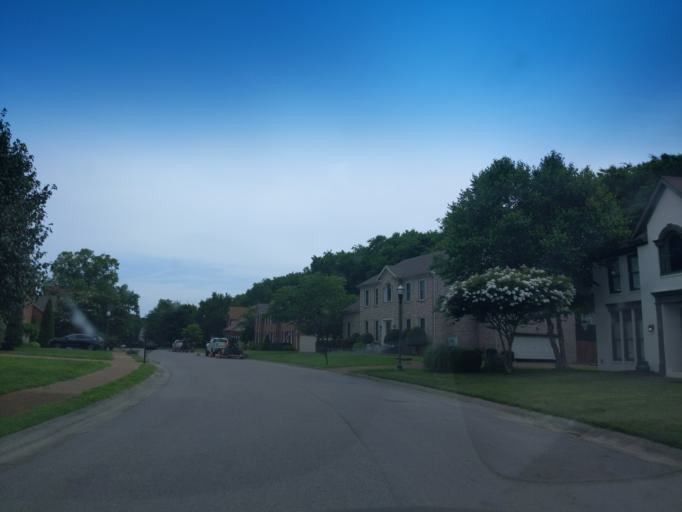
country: US
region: Tennessee
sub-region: Williamson County
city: Brentwood Estates
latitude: 36.0345
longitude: -86.7620
